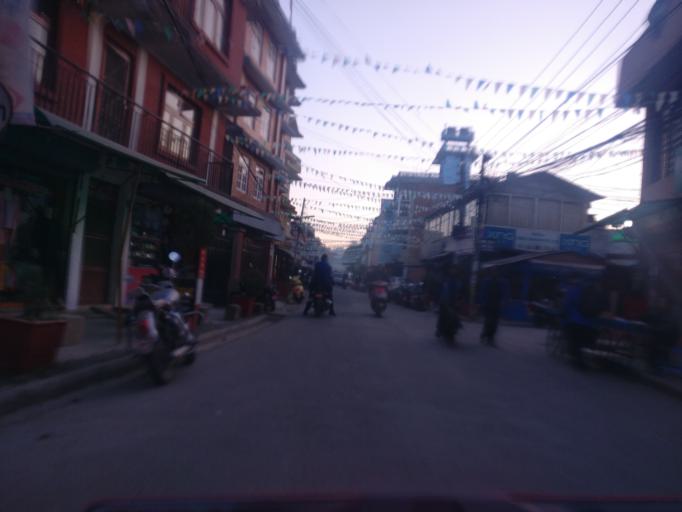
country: NP
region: Central Region
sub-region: Bagmati Zone
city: Patan
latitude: 27.6543
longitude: 85.3194
